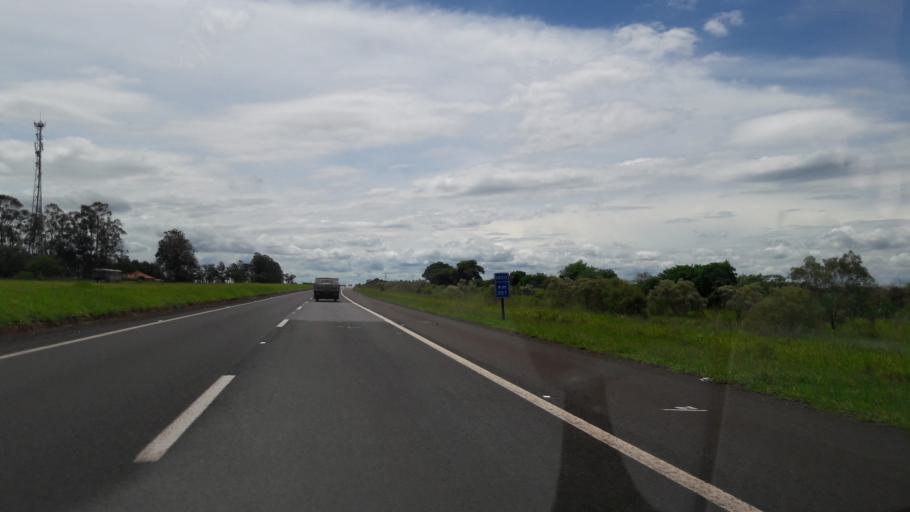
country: BR
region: Sao Paulo
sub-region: Avare
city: Avare
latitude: -22.9403
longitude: -48.9557
